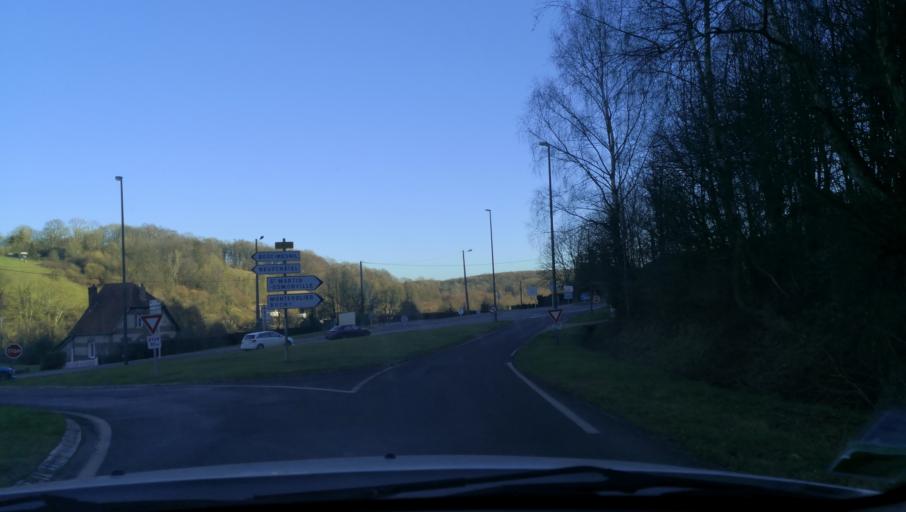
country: FR
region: Haute-Normandie
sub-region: Departement de la Seine-Maritime
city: Saint-Martin-Osmonville
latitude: 49.6456
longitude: 1.3012
